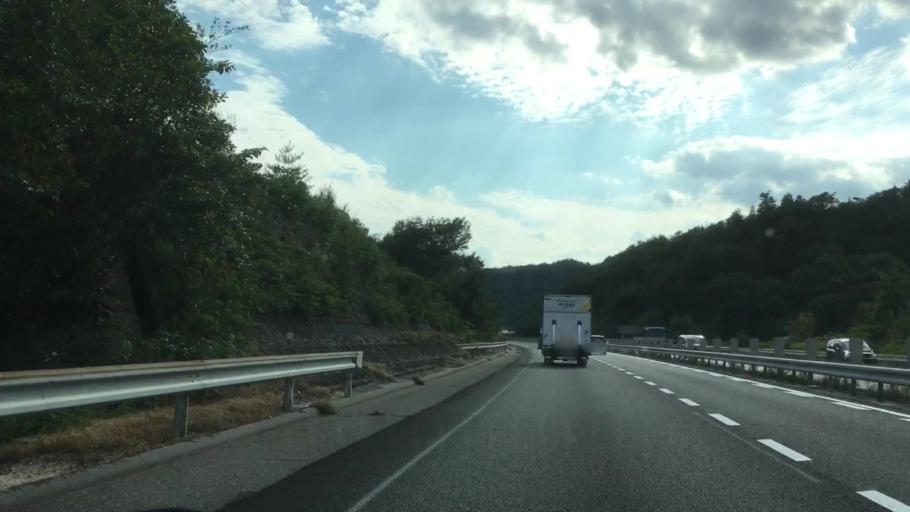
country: JP
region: Hiroshima
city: Ono-hara
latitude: 34.3187
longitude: 132.2833
